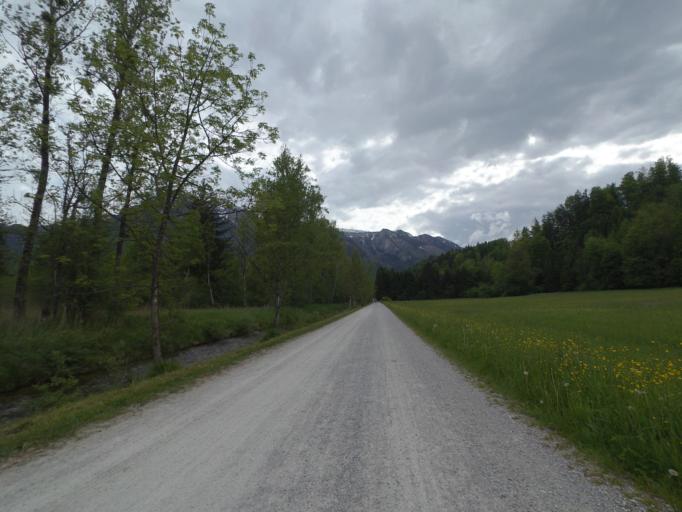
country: AT
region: Salzburg
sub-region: Politischer Bezirk Salzburg-Umgebung
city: Grodig
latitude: 47.7567
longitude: 12.9965
